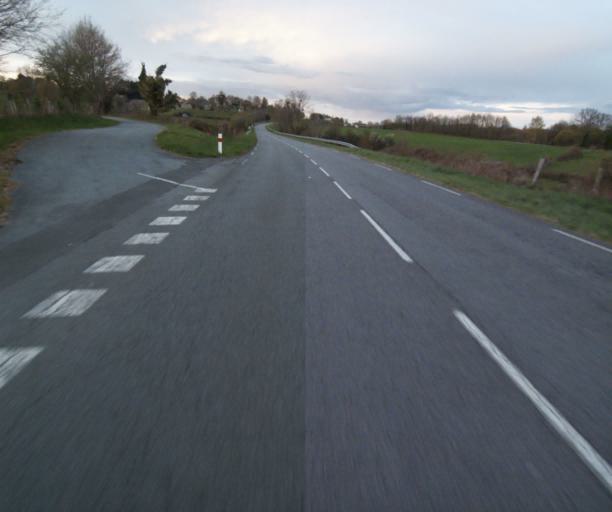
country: FR
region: Limousin
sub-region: Departement de la Correze
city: Laguenne
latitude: 45.2646
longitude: 1.8143
